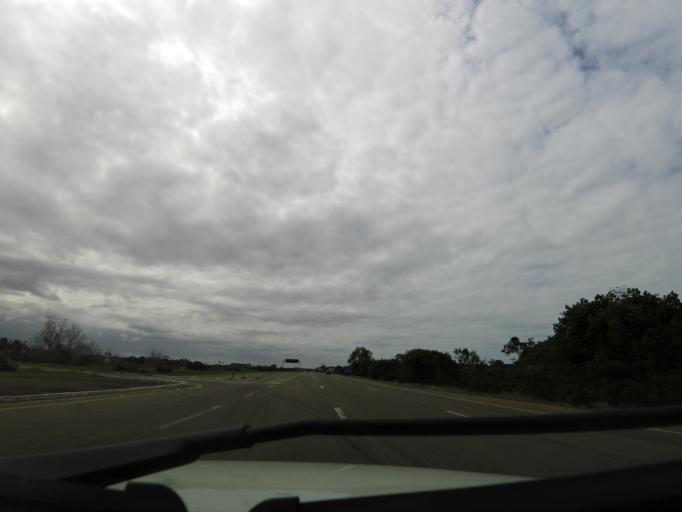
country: BR
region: Espirito Santo
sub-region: Guarapari
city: Guarapari
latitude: -20.6186
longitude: -40.4319
